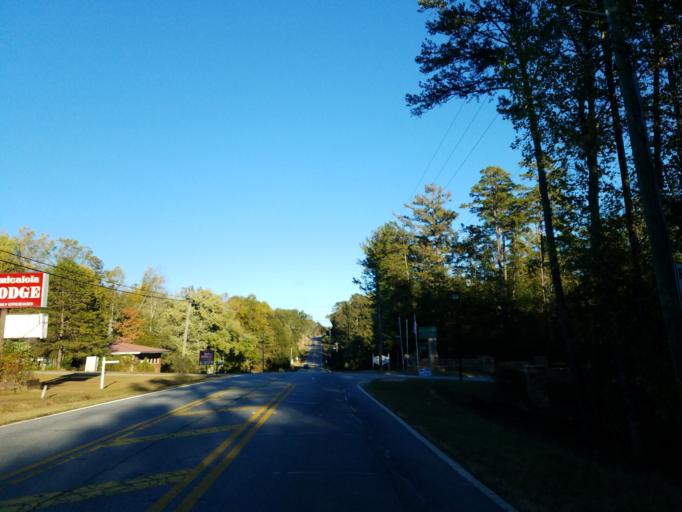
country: US
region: Georgia
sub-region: Dawson County
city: Dawsonville
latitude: 34.4211
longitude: -84.1316
